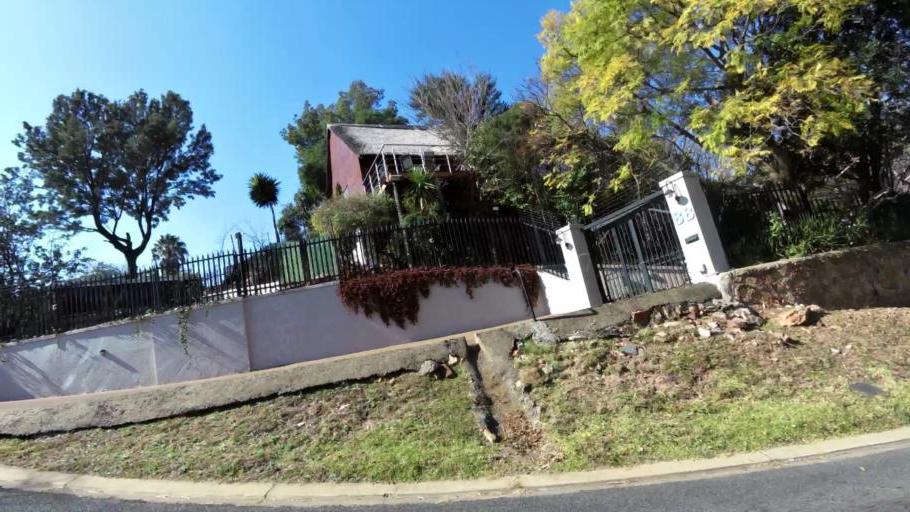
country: ZA
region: Gauteng
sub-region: City of Johannesburg Metropolitan Municipality
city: Roodepoort
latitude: -26.1471
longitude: 27.9622
